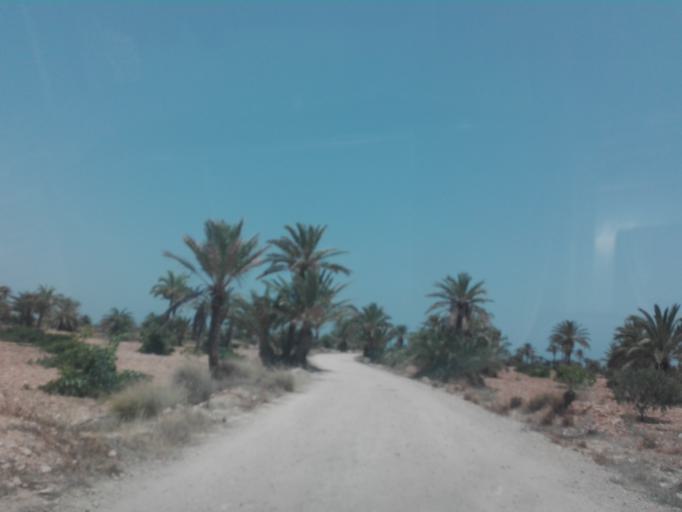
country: TN
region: Safaqis
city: Al Qarmadah
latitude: 34.6632
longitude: 11.0927
